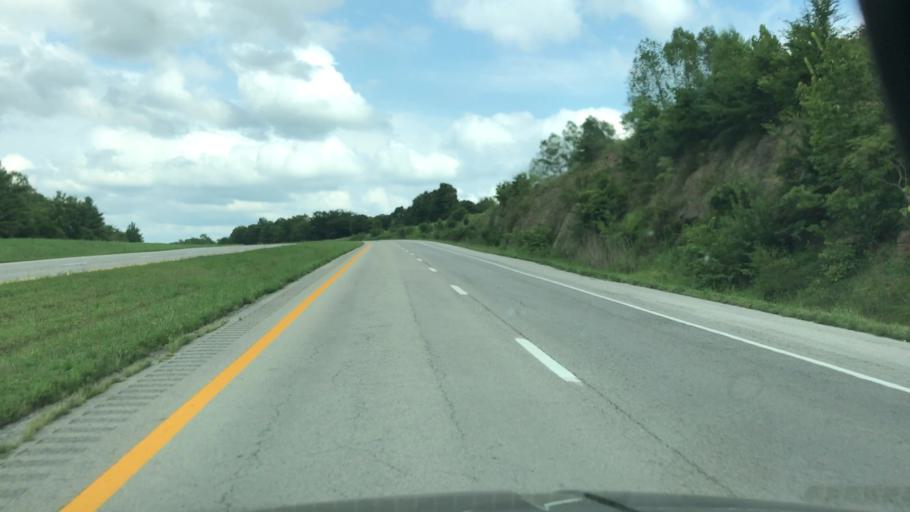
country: US
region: Kentucky
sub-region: Caldwell County
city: Princeton
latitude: 37.1405
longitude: -87.8183
